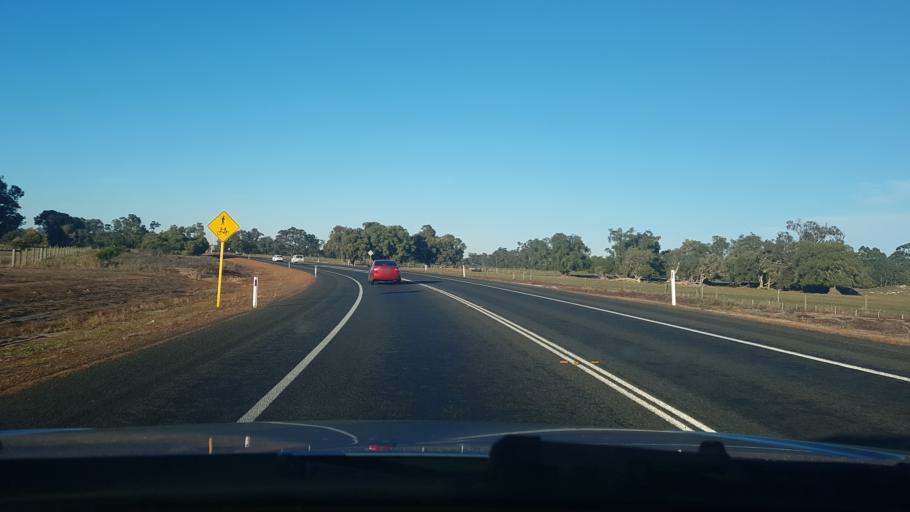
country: AU
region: Western Australia
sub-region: Busselton
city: Vasse
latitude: -33.6738
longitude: 115.2305
